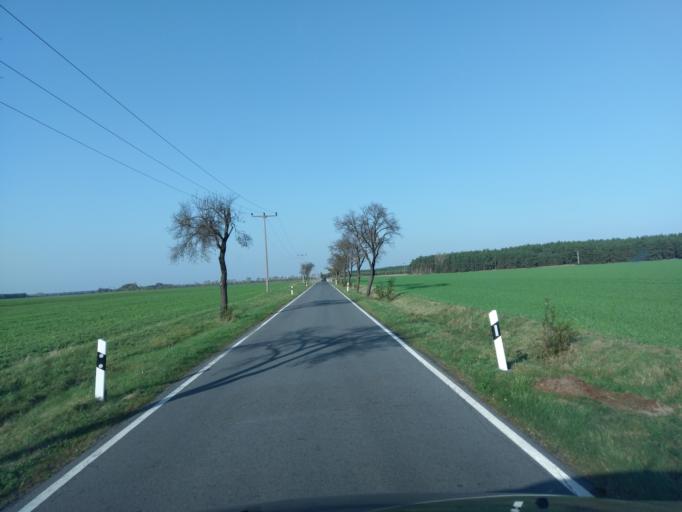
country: DE
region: Brandenburg
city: Muhlberg
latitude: 51.4787
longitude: 13.2719
